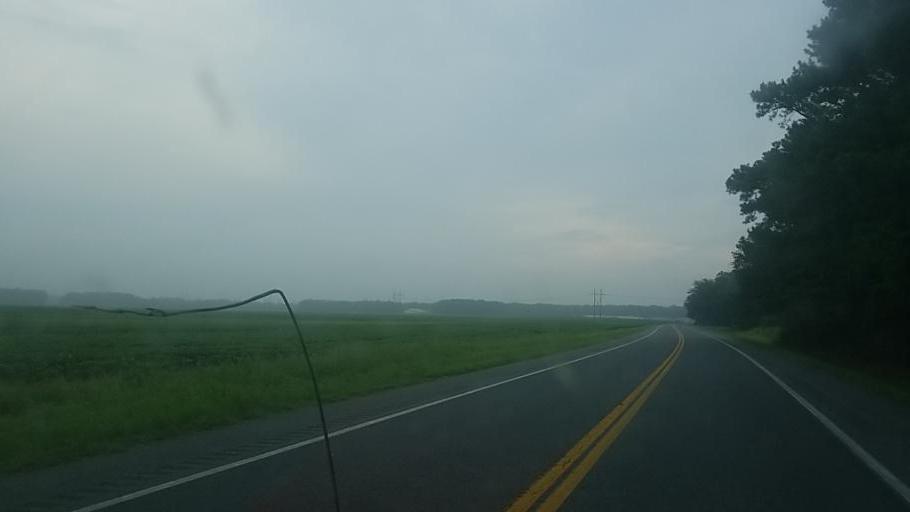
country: US
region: Maryland
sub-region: Wicomico County
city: Pittsville
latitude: 38.4519
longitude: -75.4159
